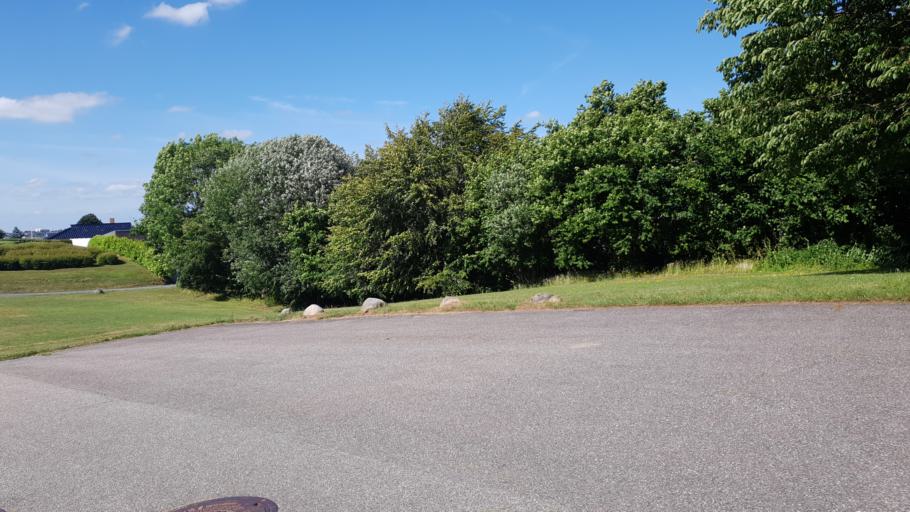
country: DK
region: South Denmark
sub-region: Fredericia Kommune
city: Snoghoj
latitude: 55.5336
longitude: 9.7335
